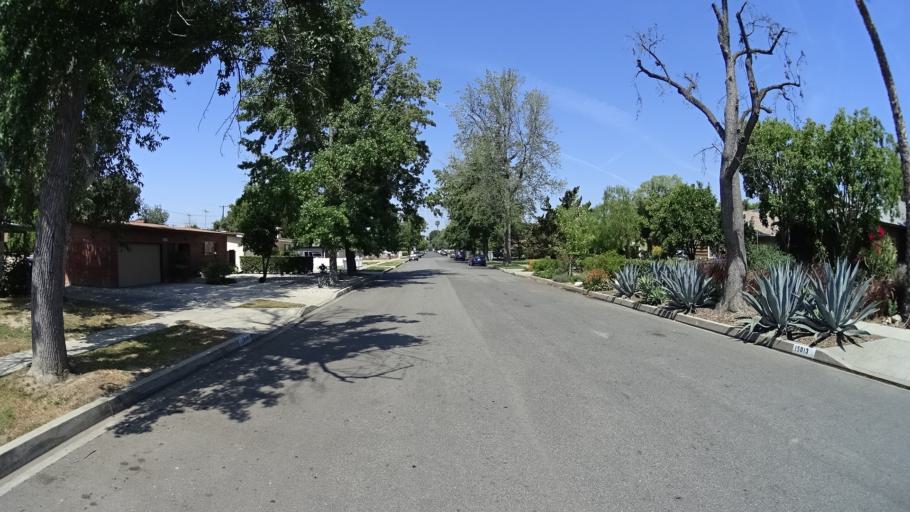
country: US
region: California
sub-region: Los Angeles County
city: Van Nuys
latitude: 34.2039
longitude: -118.4604
